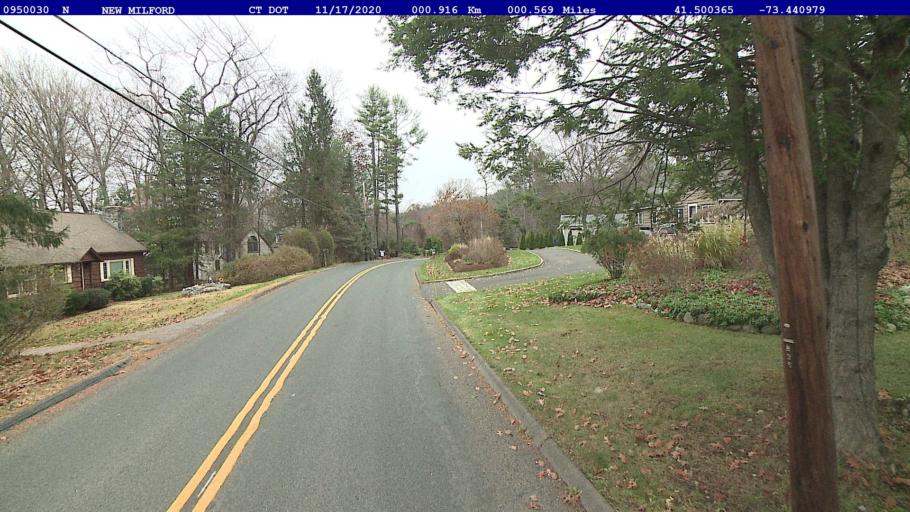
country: US
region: Connecticut
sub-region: Litchfield County
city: New Milford
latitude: 41.5004
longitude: -73.4410
